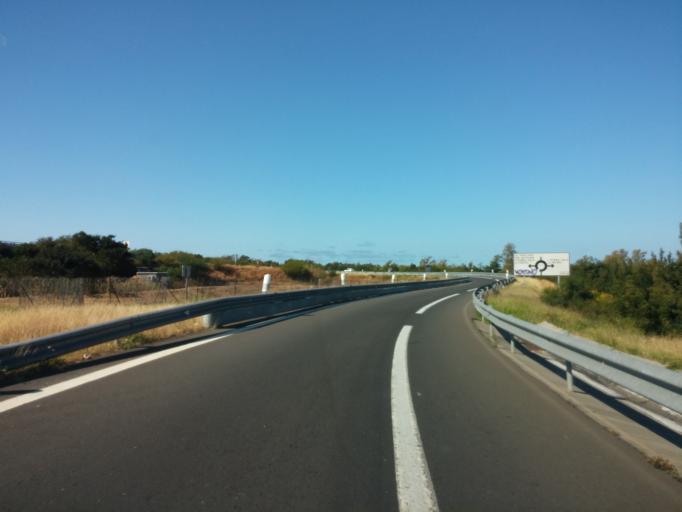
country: RE
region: Reunion
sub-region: Reunion
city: Les Avirons
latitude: -21.2621
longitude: 55.3380
